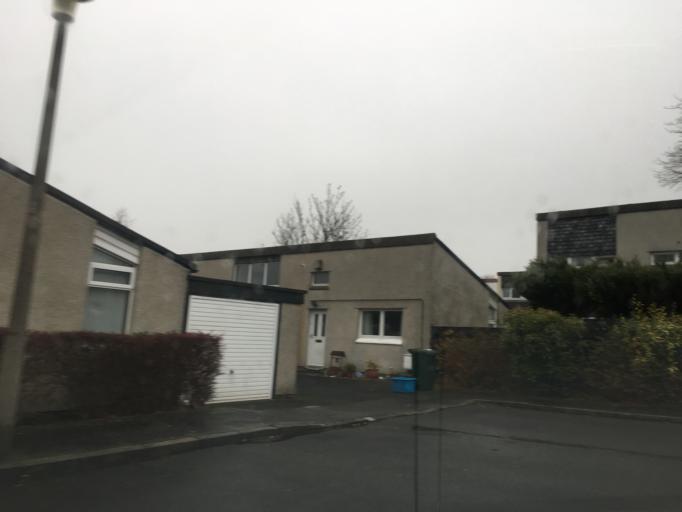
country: GB
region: Scotland
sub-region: Edinburgh
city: Currie
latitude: 55.9575
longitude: -3.3058
